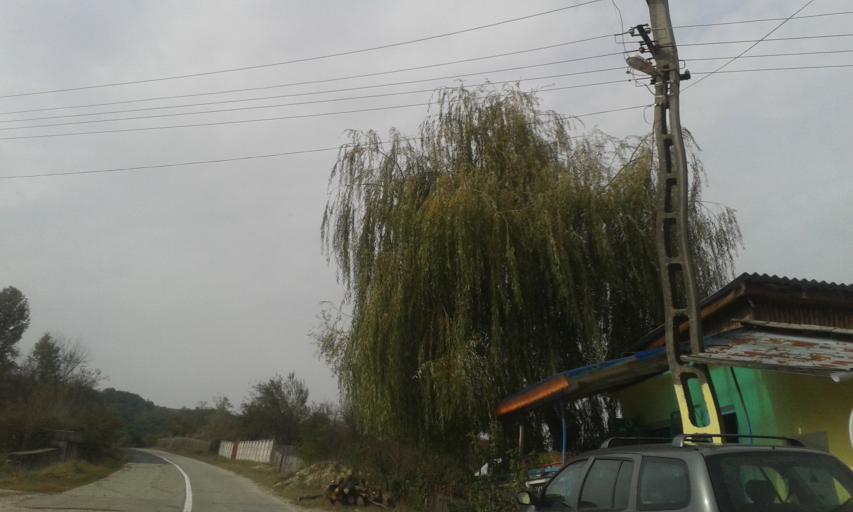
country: RO
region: Valcea
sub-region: Comuna Gradistea
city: Gradistea
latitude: 44.9162
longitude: 23.7801
